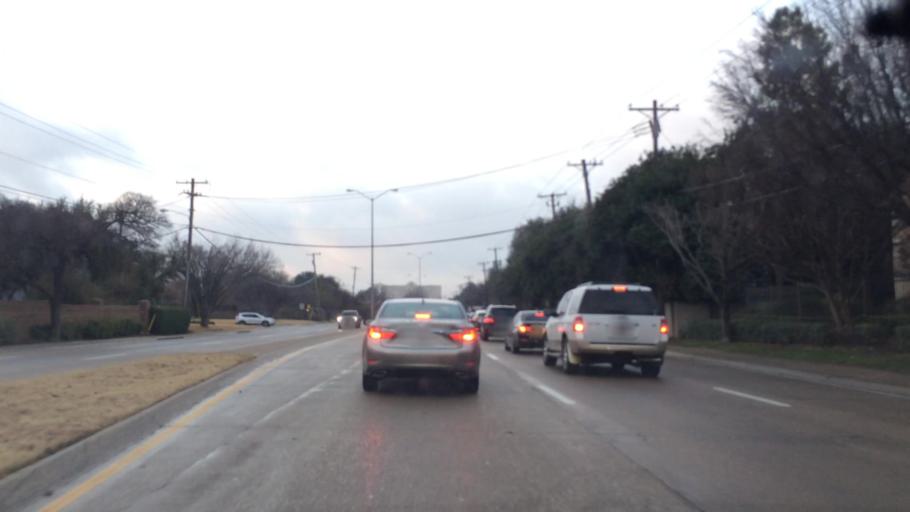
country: US
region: Texas
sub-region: Dallas County
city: Addison
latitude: 32.9606
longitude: -96.8046
